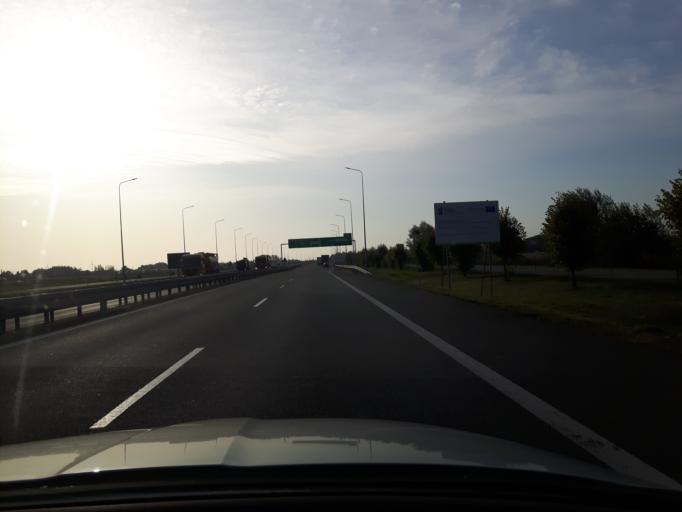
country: PL
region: Masovian Voivodeship
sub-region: Powiat radomski
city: Jedlinsk
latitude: 51.5376
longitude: 21.0698
